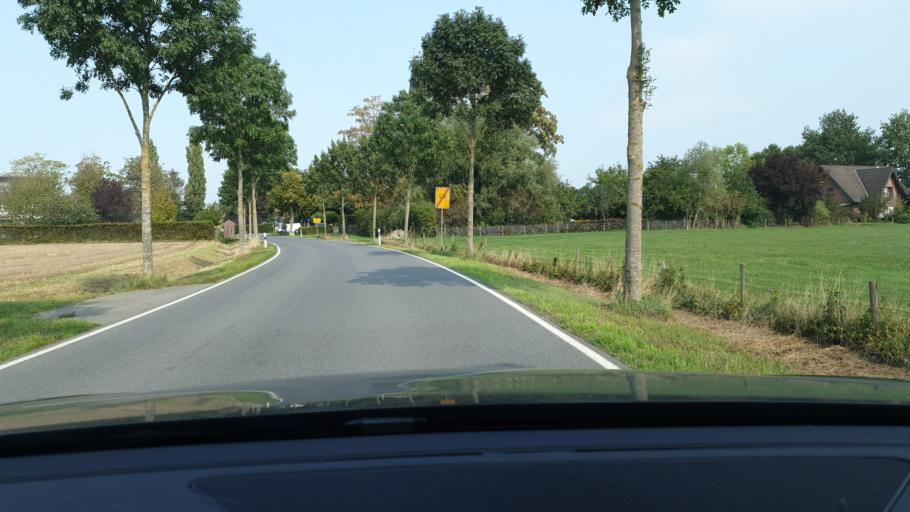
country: DE
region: North Rhine-Westphalia
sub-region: Regierungsbezirk Dusseldorf
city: Kranenburg
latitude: 51.8241
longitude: 6.0184
